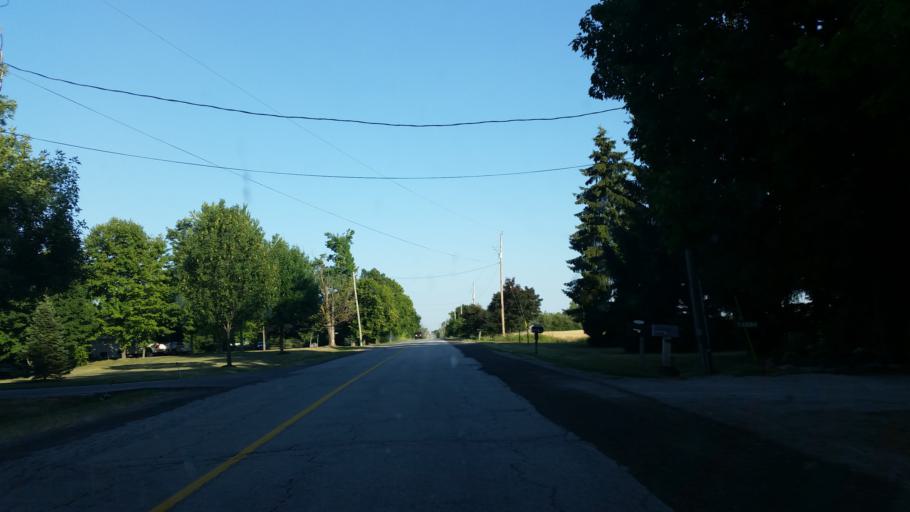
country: CA
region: Ontario
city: Brampton
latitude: 43.7904
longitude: -79.8541
